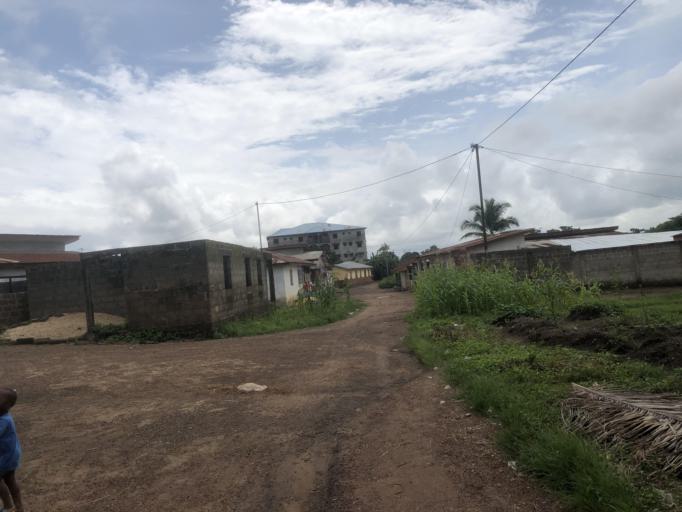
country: SL
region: Northern Province
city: Magburaka
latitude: 8.7186
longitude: -11.9343
